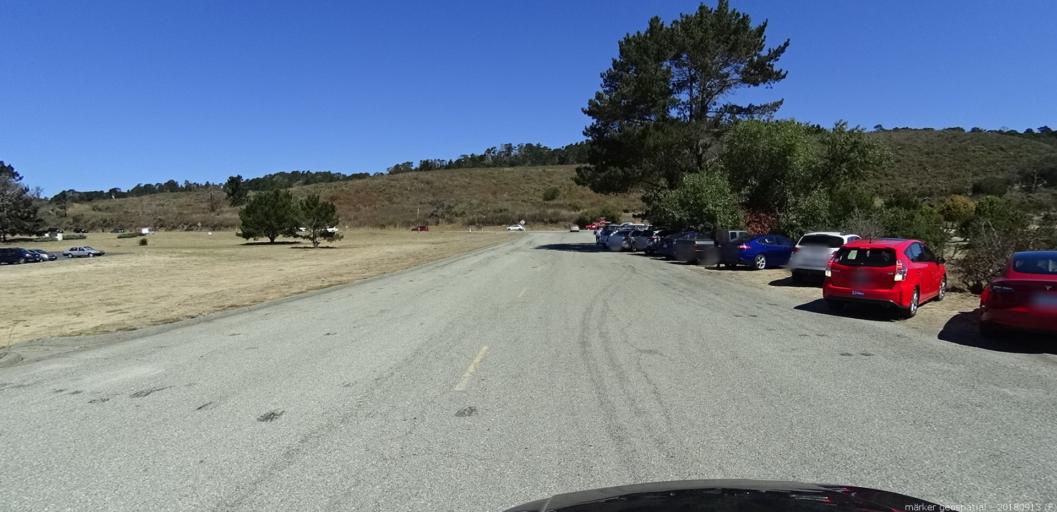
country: US
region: California
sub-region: Monterey County
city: Carmel-by-the-Sea
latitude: 36.5418
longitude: -121.8922
